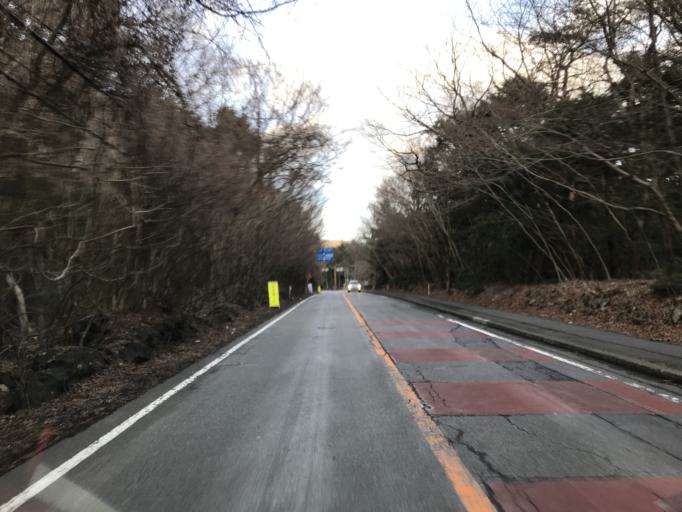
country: JP
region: Yamanashi
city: Fujikawaguchiko
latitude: 35.4788
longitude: 138.6078
